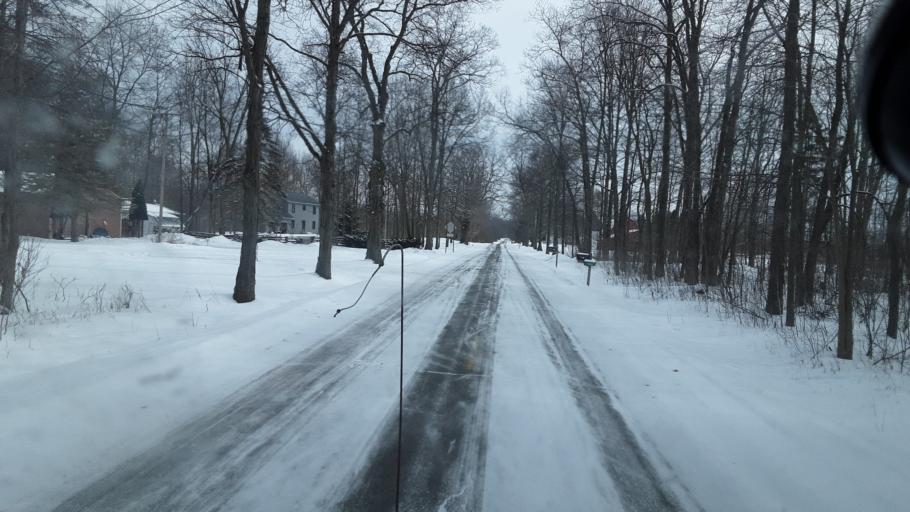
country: US
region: Michigan
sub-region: Ingham County
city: Leslie
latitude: 42.5021
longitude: -84.3877
